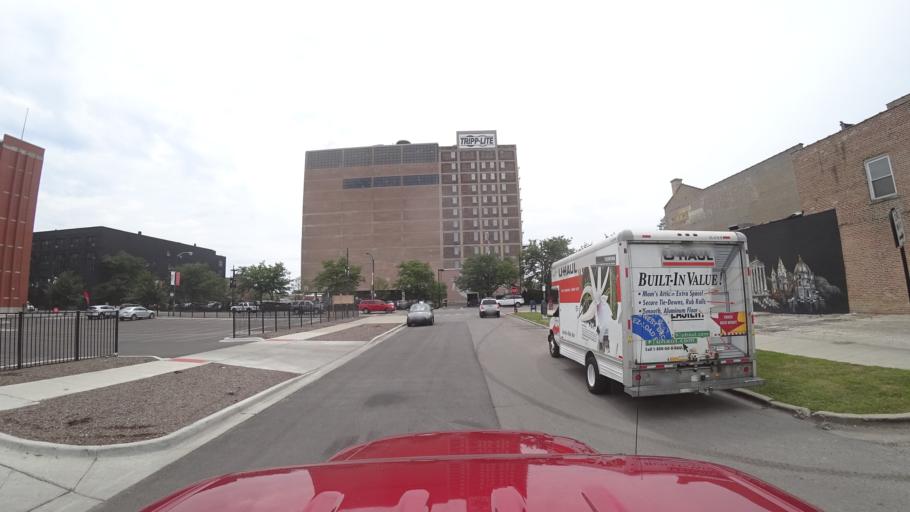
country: US
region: Illinois
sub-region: Cook County
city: Chicago
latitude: 41.8311
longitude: -87.6534
